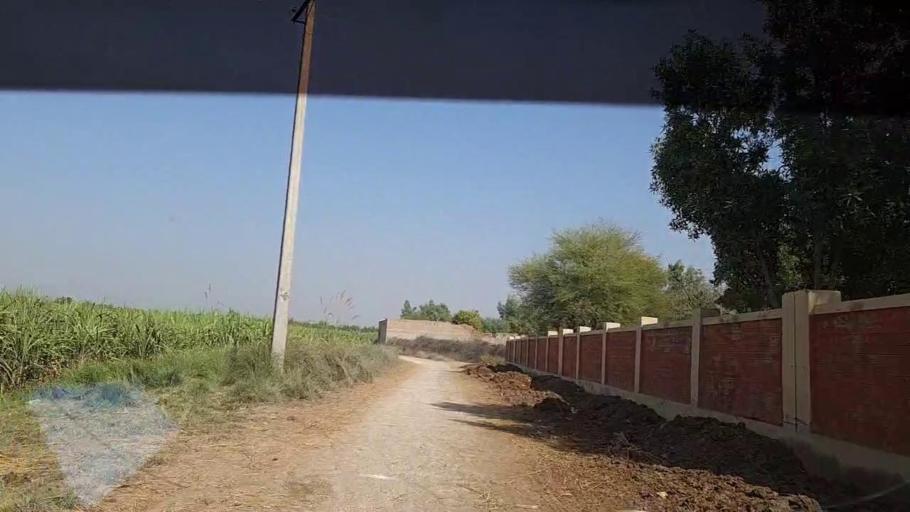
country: PK
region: Sindh
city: Naudero
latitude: 27.6471
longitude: 68.3664
